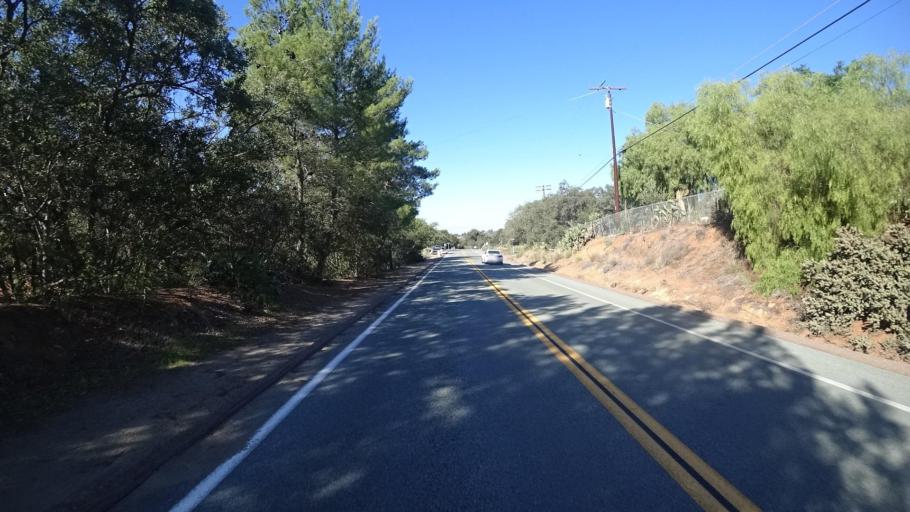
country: US
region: California
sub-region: San Diego County
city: Jamul
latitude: 32.7297
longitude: -116.8419
